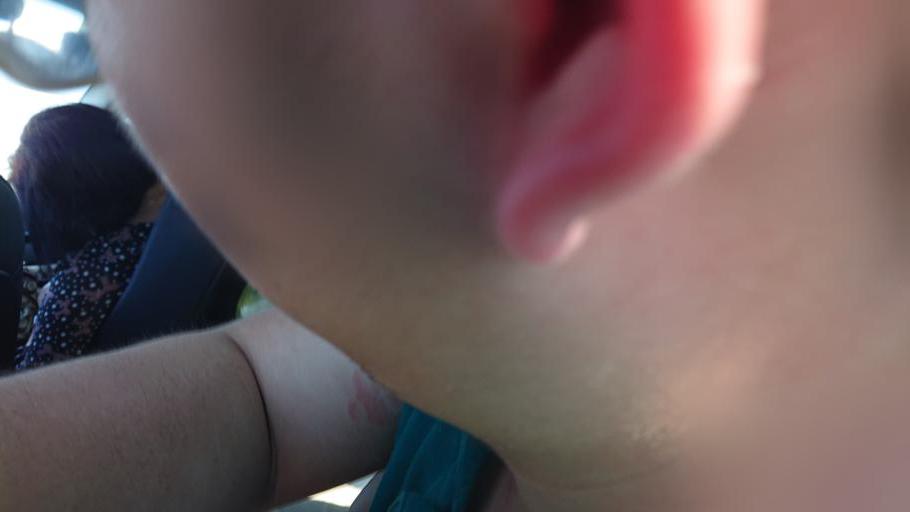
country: TW
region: Taiwan
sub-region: Chiayi
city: Taibao
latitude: 23.7020
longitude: 120.1806
